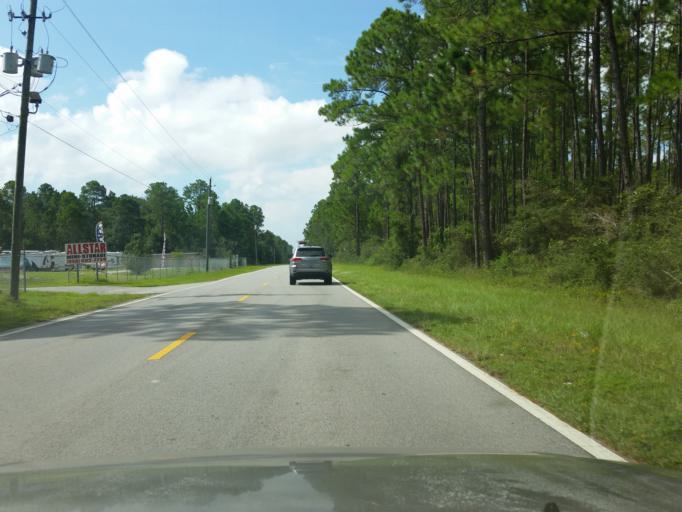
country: US
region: Florida
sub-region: Escambia County
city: Myrtle Grove
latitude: 30.3384
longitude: -87.4033
